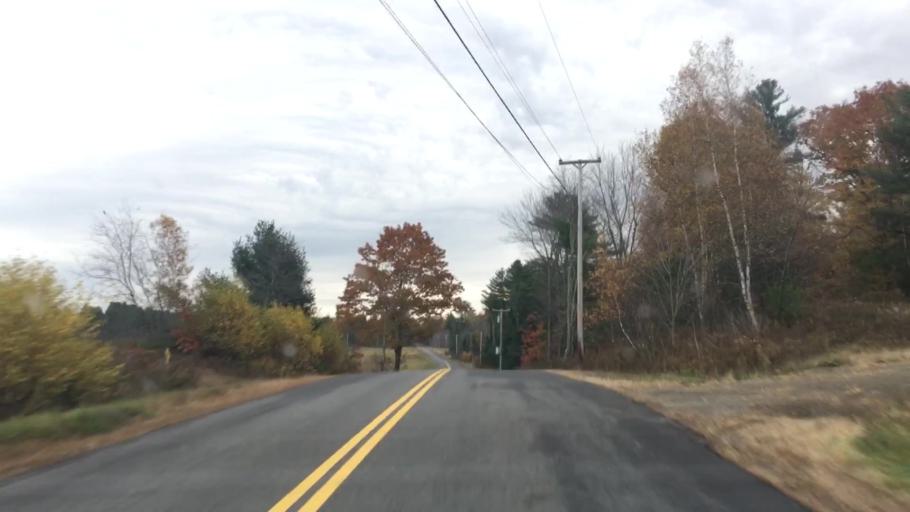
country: US
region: Maine
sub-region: Kennebec County
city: Pittston
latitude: 44.1690
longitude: -69.7155
